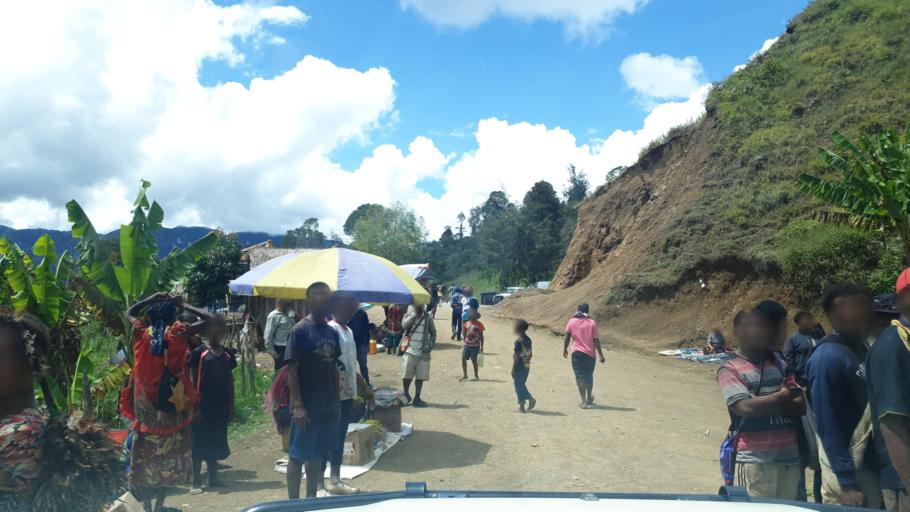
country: PG
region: Eastern Highlands
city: Goroka
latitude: -6.2785
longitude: 145.1846
